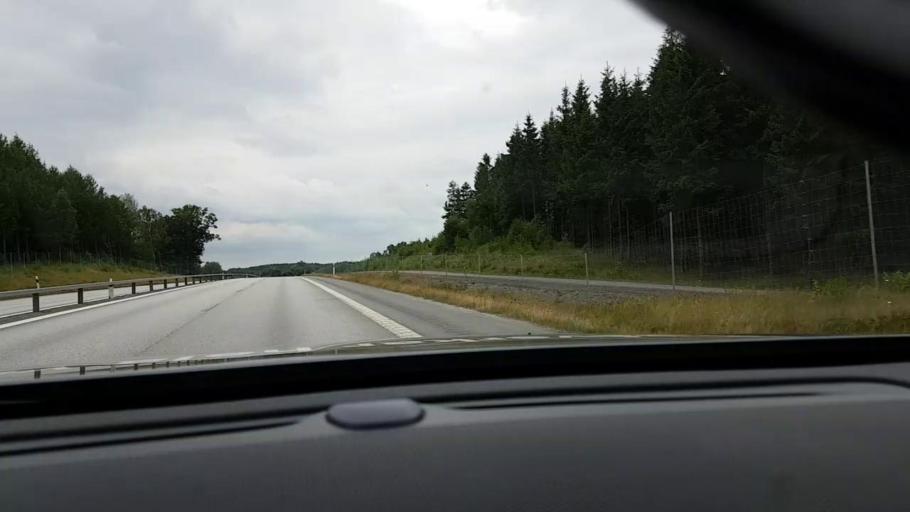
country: SE
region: Skane
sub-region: Horby Kommun
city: Hoerby
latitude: 55.8801
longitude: 13.7129
